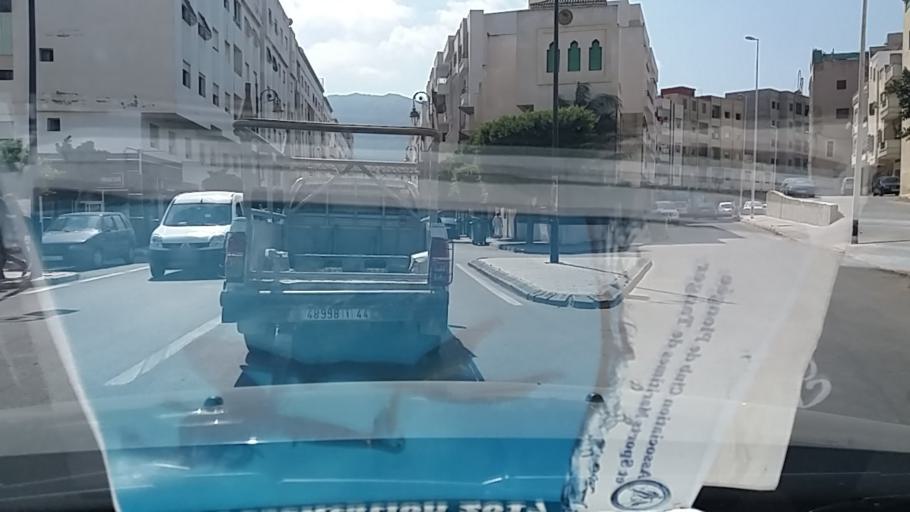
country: MA
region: Tanger-Tetouan
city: Tetouan
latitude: 35.5674
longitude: -5.3568
